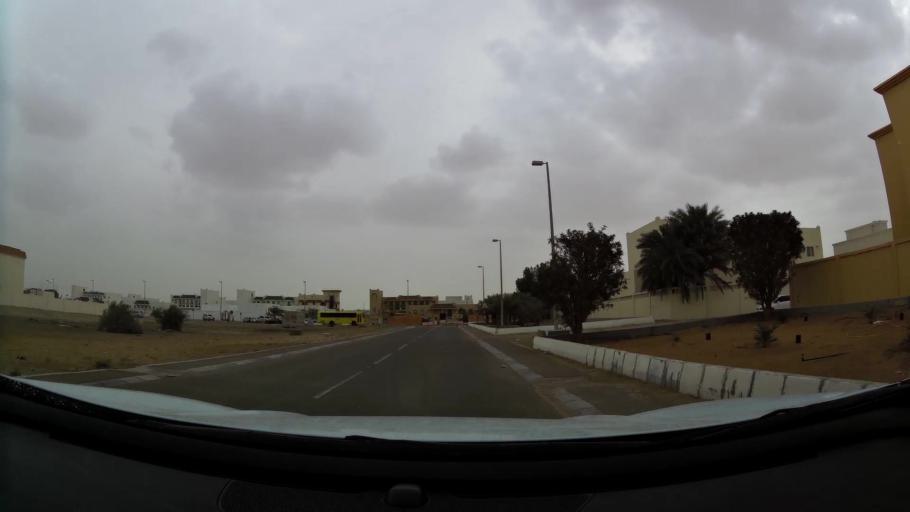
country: AE
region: Abu Dhabi
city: Abu Dhabi
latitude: 24.3569
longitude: 54.6527
